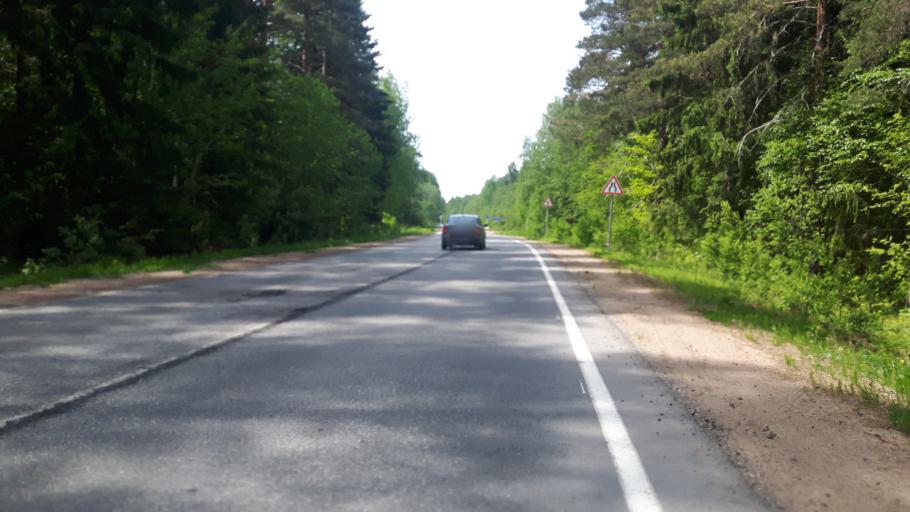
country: RU
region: Leningrad
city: Ust'-Luga
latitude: 59.6464
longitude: 28.2127
